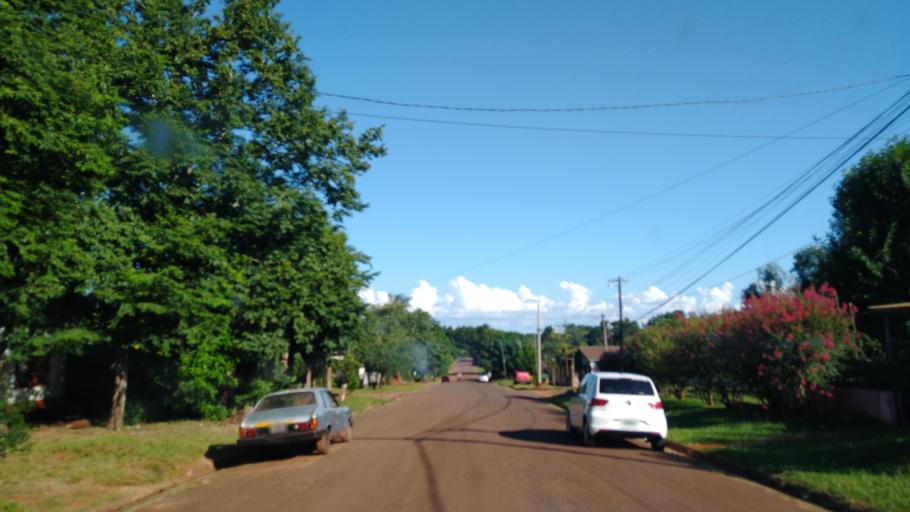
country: AR
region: Misiones
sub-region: Departamento de San Ignacio
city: San Ignacio
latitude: -27.2621
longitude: -55.5394
